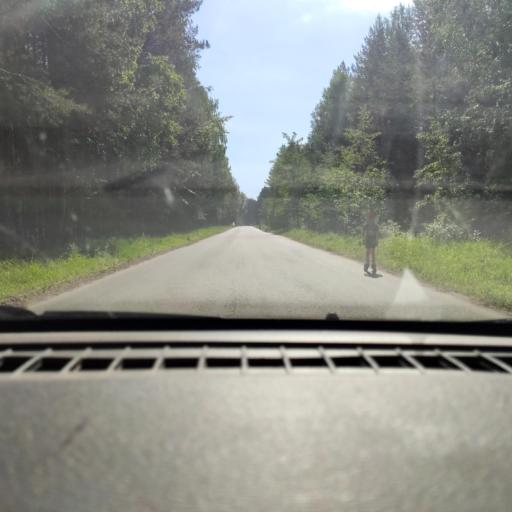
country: RU
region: Perm
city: Overyata
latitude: 57.9987
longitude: 55.8735
